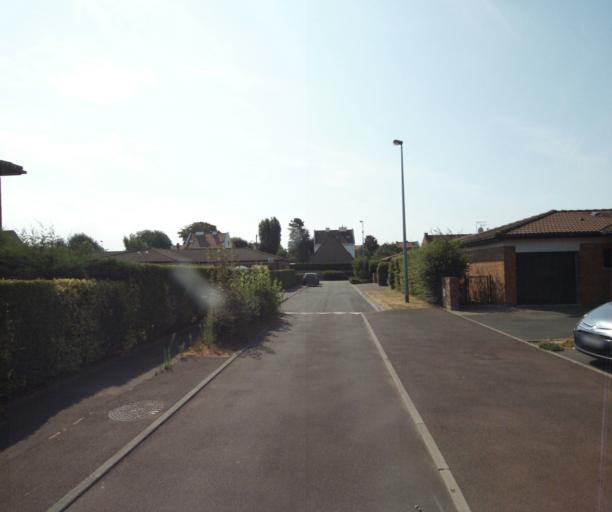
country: FR
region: Nord-Pas-de-Calais
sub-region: Departement du Nord
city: Comines
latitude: 50.7656
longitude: 3.0155
